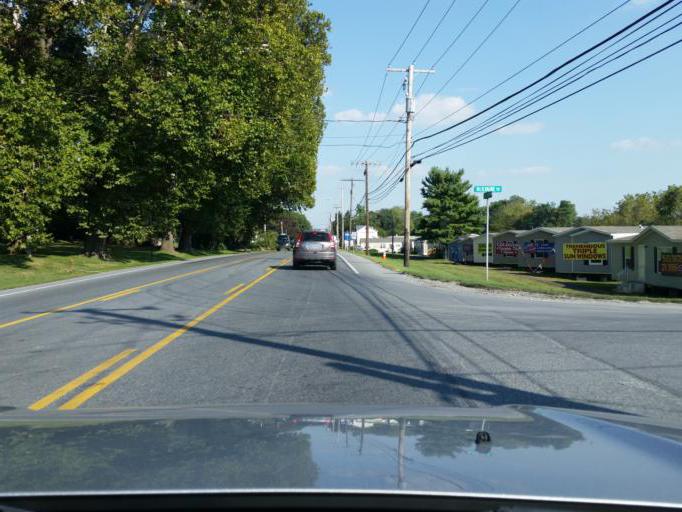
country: US
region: Pennsylvania
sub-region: Lancaster County
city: Paradise
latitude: 40.0023
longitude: -76.0923
